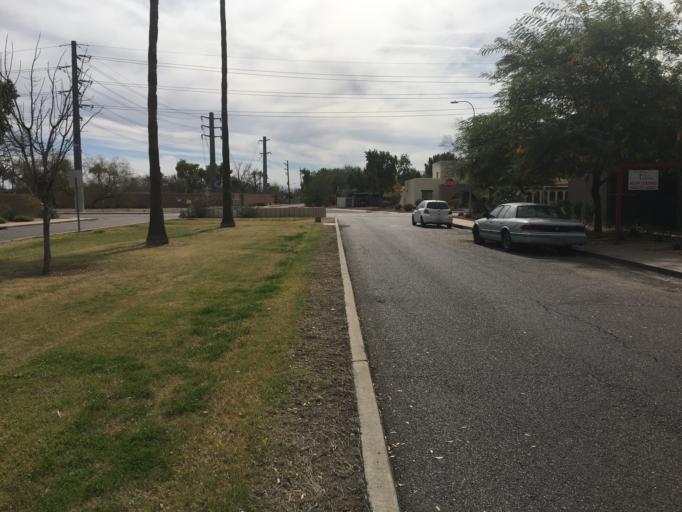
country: US
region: Arizona
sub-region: Maricopa County
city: Phoenix
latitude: 33.5318
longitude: -112.0956
